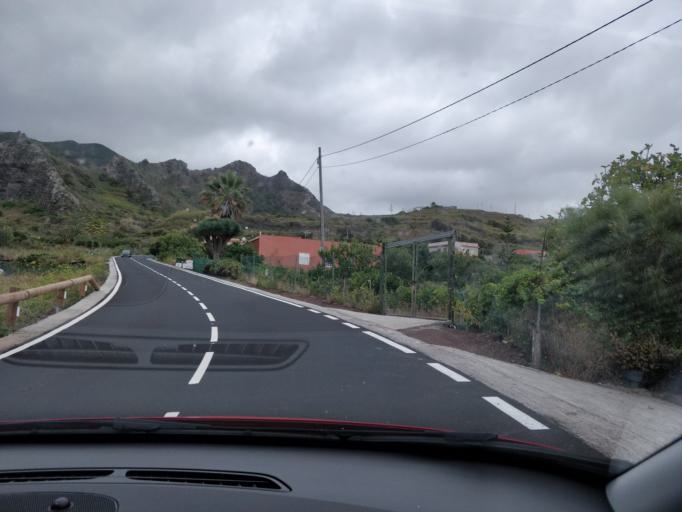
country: ES
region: Canary Islands
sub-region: Provincia de Santa Cruz de Tenerife
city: Tanque
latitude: 28.3515
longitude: -16.8448
